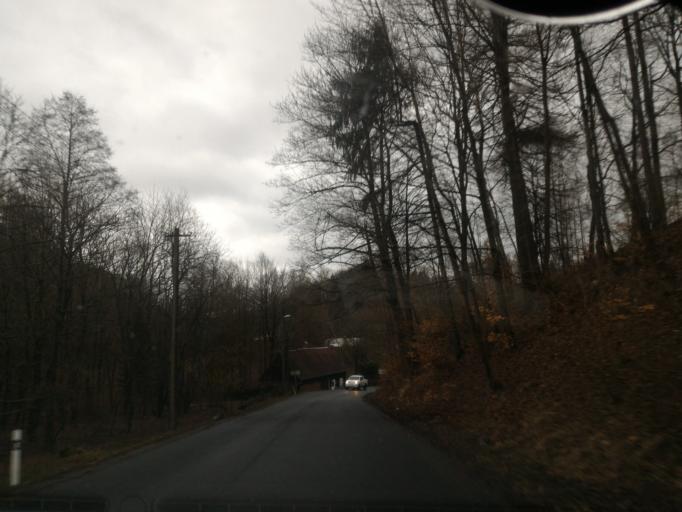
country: CZ
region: Ustecky
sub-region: Okres Decin
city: Krasna Lipa
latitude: 50.9230
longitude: 14.4900
